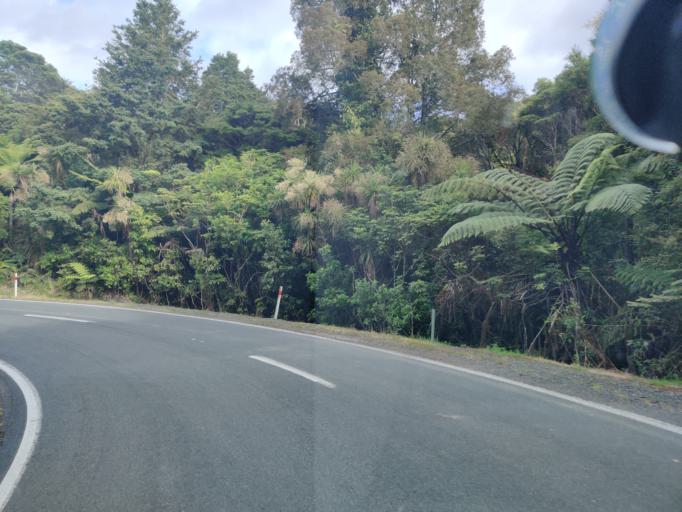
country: NZ
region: Northland
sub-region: Whangarei
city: Ngunguru
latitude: -35.5821
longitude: 174.4256
